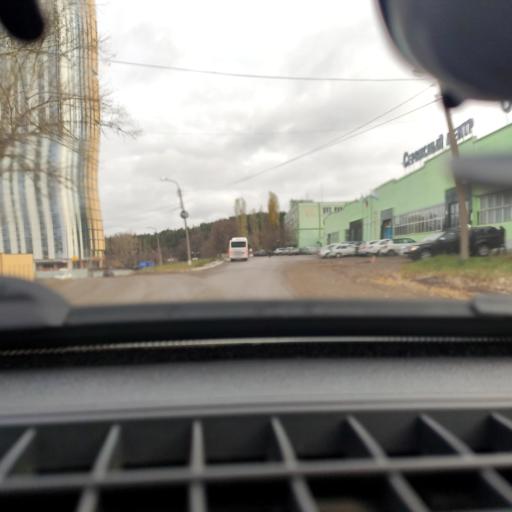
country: RU
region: Bashkortostan
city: Ufa
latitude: 54.7232
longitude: 55.9988
